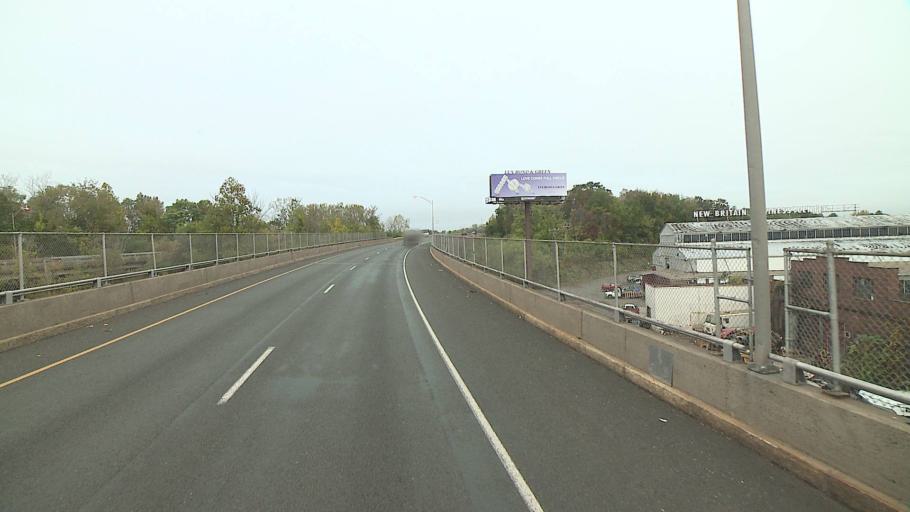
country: US
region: Connecticut
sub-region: Hartford County
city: Kensington
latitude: 41.6482
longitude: -72.7670
